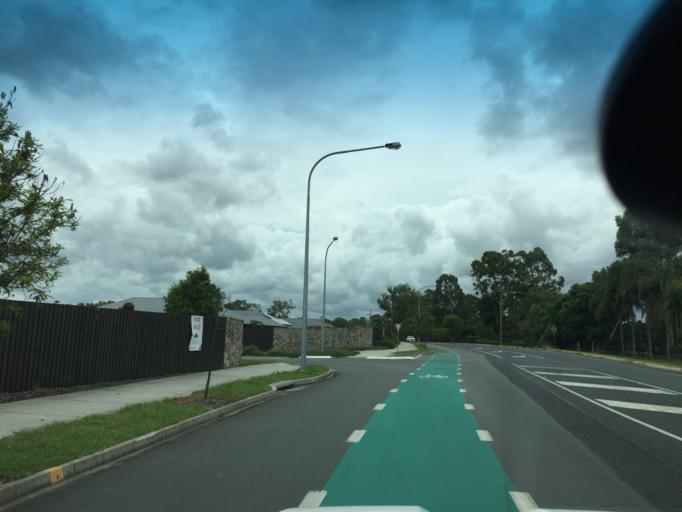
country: AU
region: Queensland
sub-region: Moreton Bay
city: Caboolture
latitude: -27.0651
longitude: 152.9337
